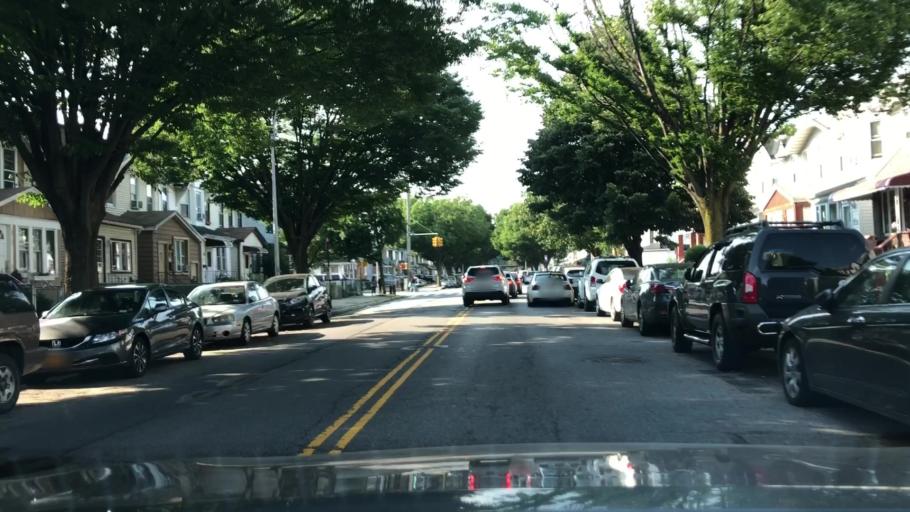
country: US
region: New York
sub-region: Queens County
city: Borough of Queens
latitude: 40.6819
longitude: -73.8297
